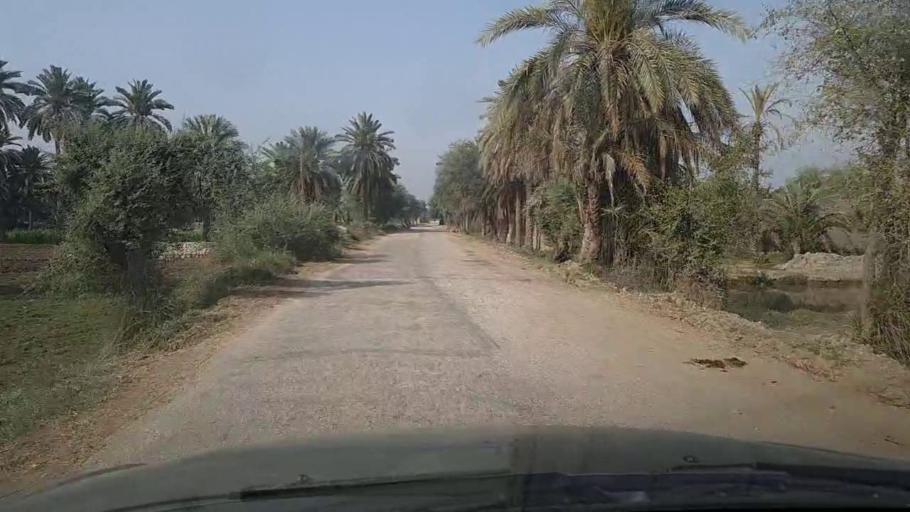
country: PK
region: Sindh
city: Pir jo Goth
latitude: 27.5444
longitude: 68.5246
